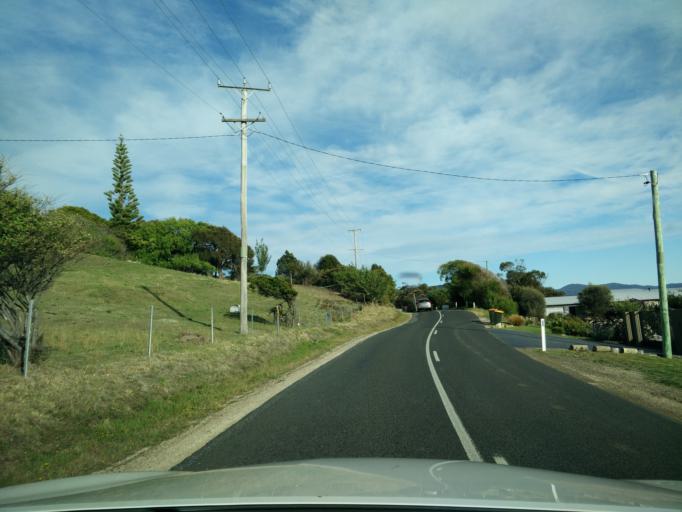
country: AU
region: Tasmania
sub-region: Break O'Day
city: St Helens
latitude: -41.8589
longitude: 148.2761
